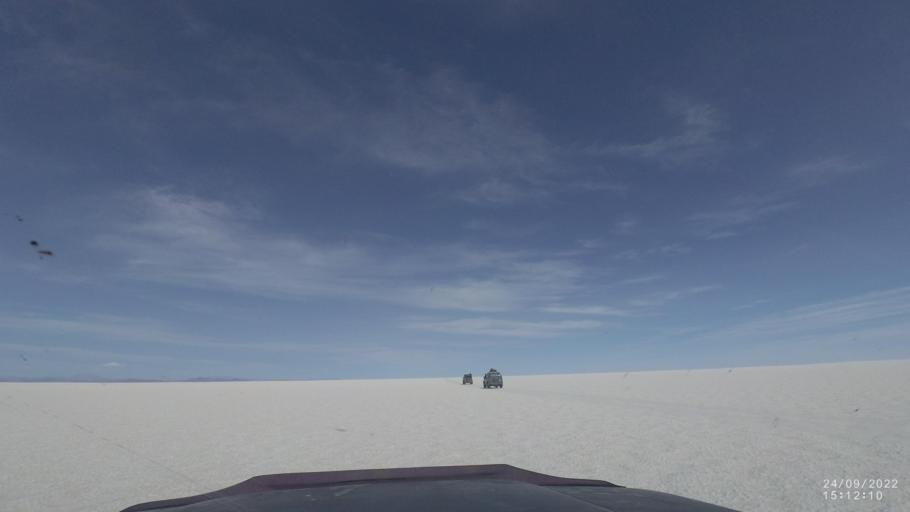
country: BO
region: Potosi
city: Colchani
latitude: -19.9487
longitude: -67.4726
